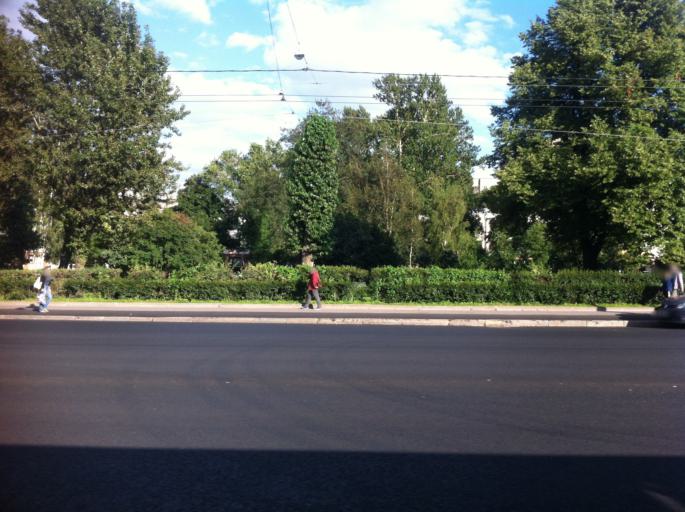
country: RU
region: St.-Petersburg
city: Avtovo
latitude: 59.8788
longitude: 30.2598
